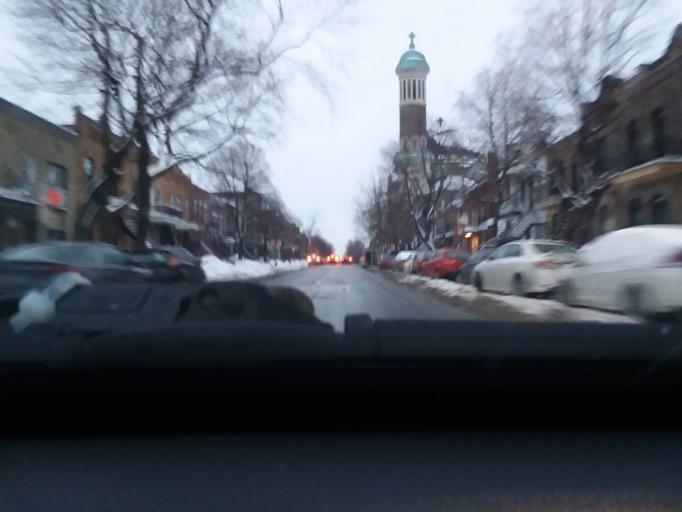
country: CA
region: Quebec
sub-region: Montreal
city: Montreal
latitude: 45.5256
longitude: -73.6020
